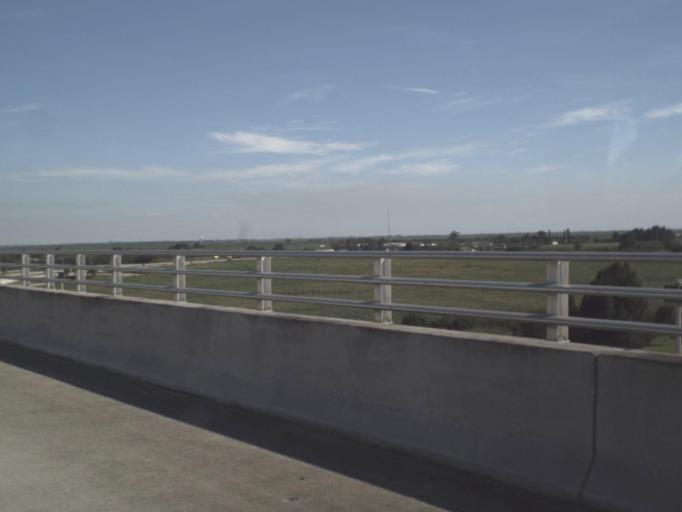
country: US
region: Florida
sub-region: Glades County
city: Moore Haven
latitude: 26.8331
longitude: -81.0888
